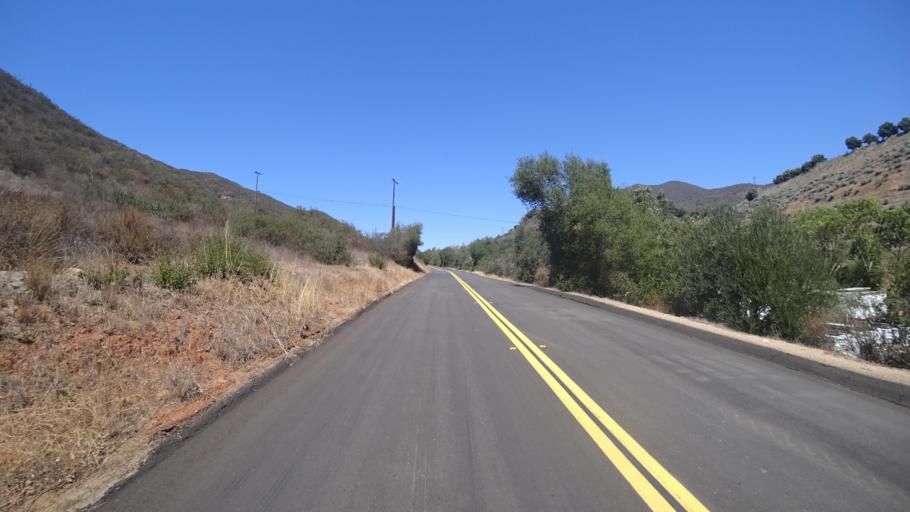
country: US
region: California
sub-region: San Diego County
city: Rainbow
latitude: 33.3641
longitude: -117.1380
